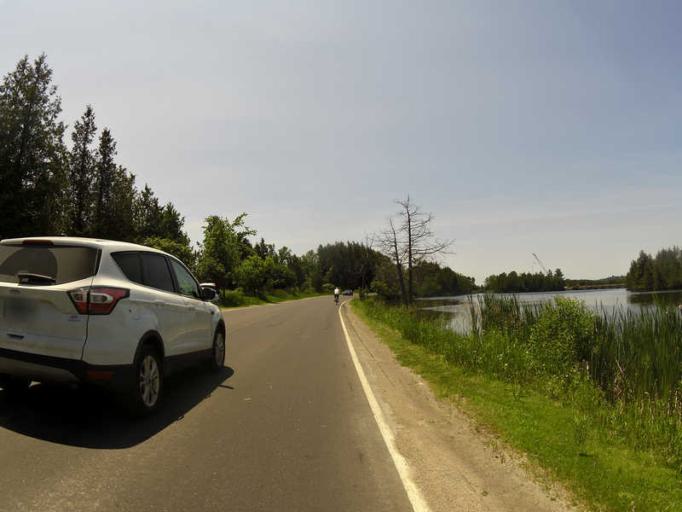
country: CA
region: Ontario
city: Peterborough
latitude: 44.3928
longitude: -78.2658
